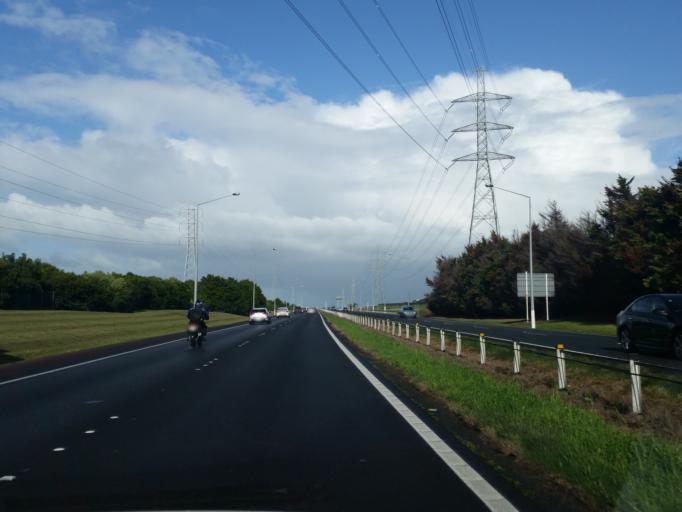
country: NZ
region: Auckland
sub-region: Auckland
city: Papakura
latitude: -37.0619
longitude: 174.9243
